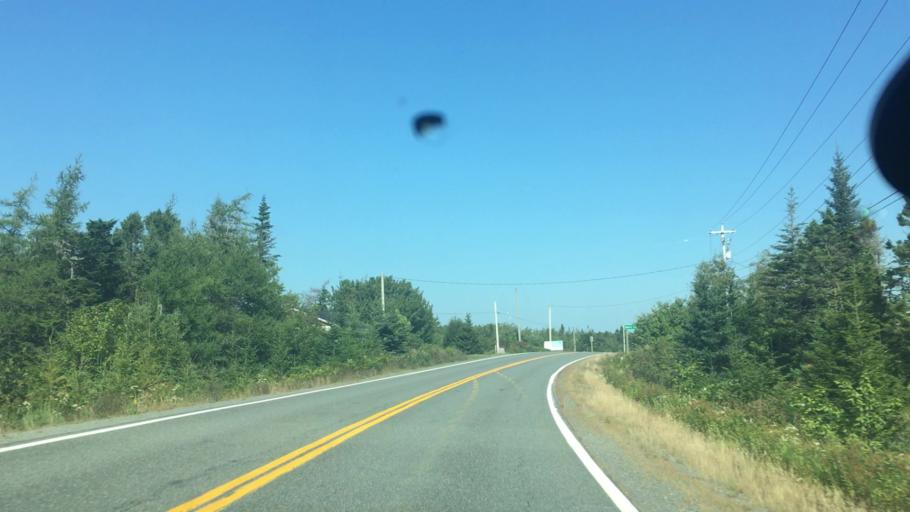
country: CA
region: Nova Scotia
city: Antigonish
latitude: 44.9974
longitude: -62.0997
